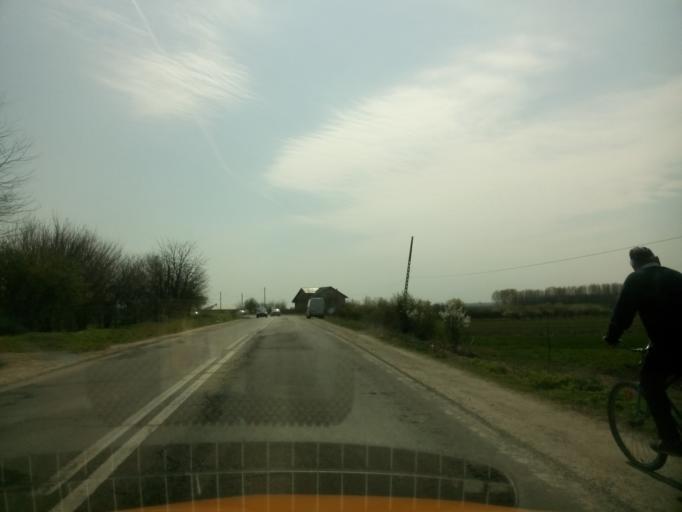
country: RO
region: Calarasi
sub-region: Comuna Soldanu
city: Negoesti
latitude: 44.2263
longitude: 26.5094
